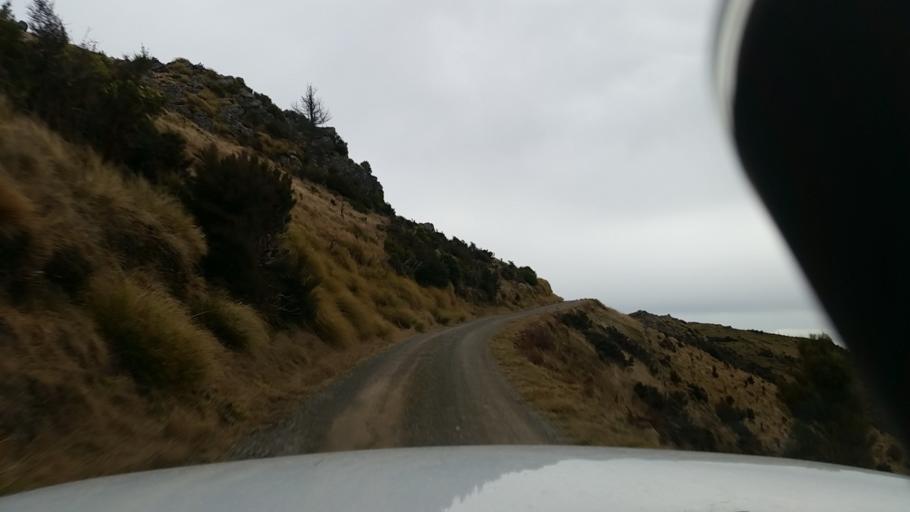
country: NZ
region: Canterbury
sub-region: Christchurch City
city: Christchurch
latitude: -43.8111
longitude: 172.8269
